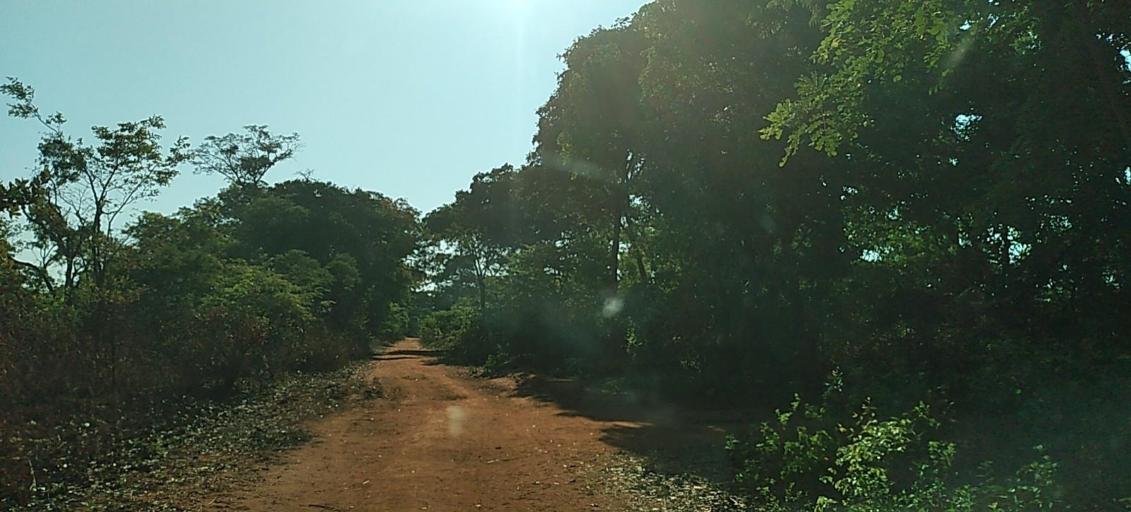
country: ZM
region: Copperbelt
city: Luanshya
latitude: -13.4588
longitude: 28.8260
